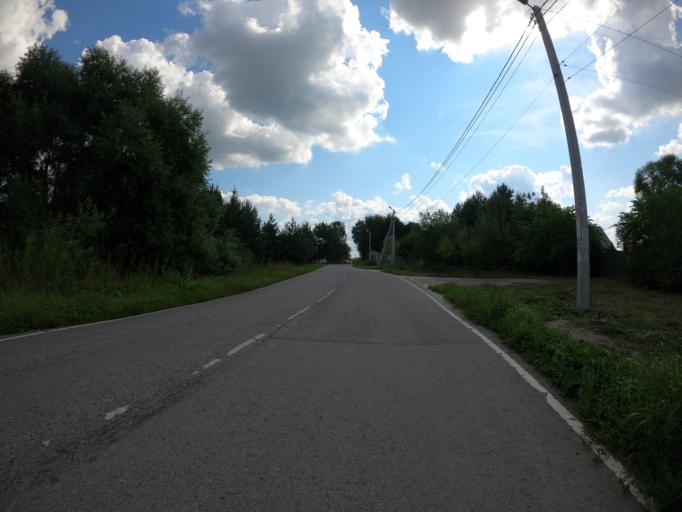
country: RU
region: Moskovskaya
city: Troitskoye
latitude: 55.2487
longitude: 38.5771
